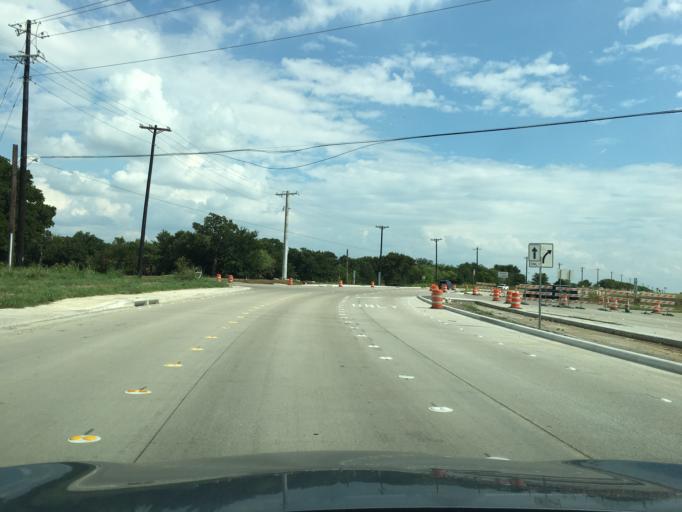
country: US
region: Texas
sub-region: Denton County
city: Oak Point
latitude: 33.1962
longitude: -96.9773
